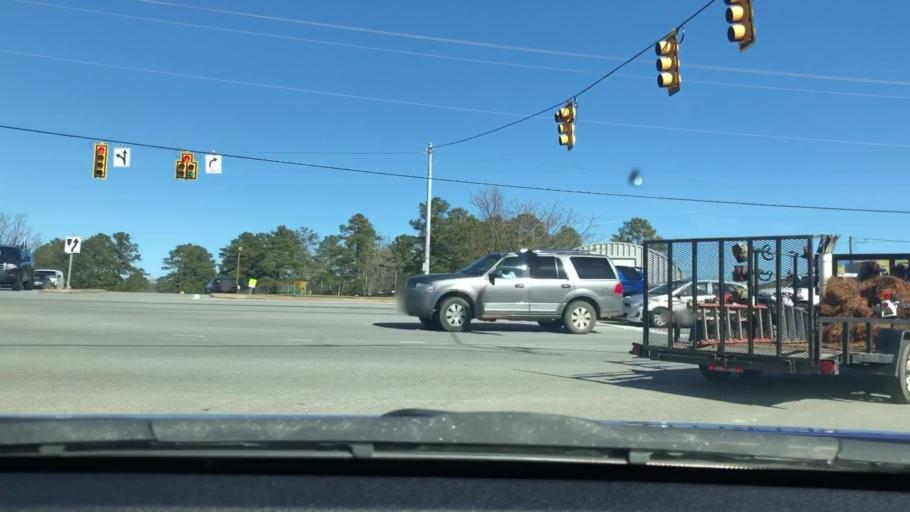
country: US
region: South Carolina
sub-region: Lexington County
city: Oak Grove
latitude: 34.0136
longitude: -81.1526
